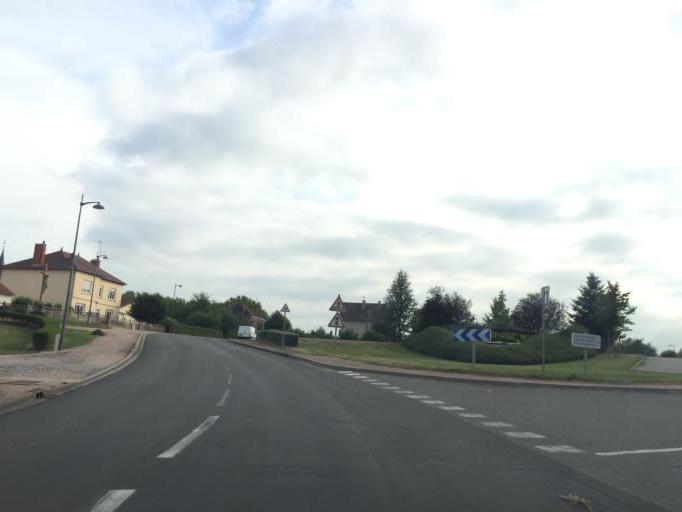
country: FR
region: Auvergne
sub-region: Departement de l'Allier
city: Molinet
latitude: 46.4670
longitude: 3.9377
